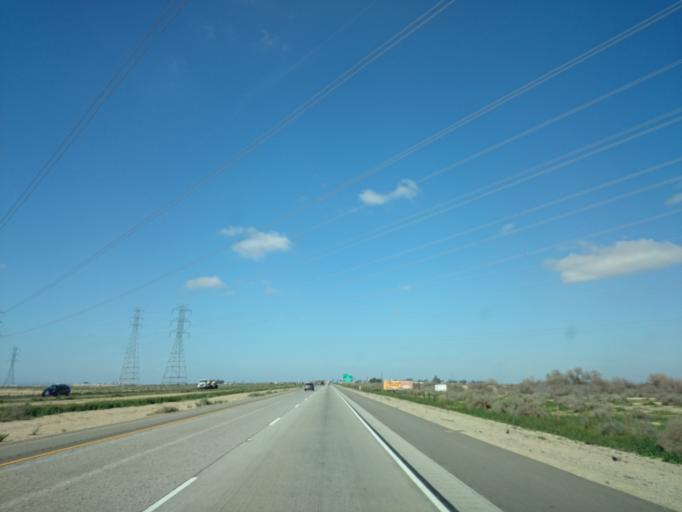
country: US
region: California
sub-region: Kern County
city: Buttonwillow
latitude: 35.3870
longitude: -119.3807
